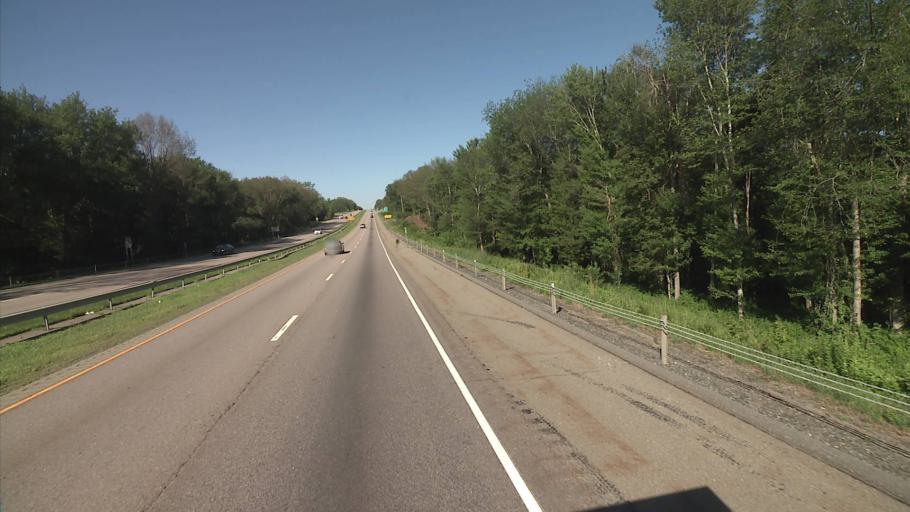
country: US
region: Connecticut
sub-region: New London County
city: Oxoboxo River
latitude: 41.3992
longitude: -72.1588
